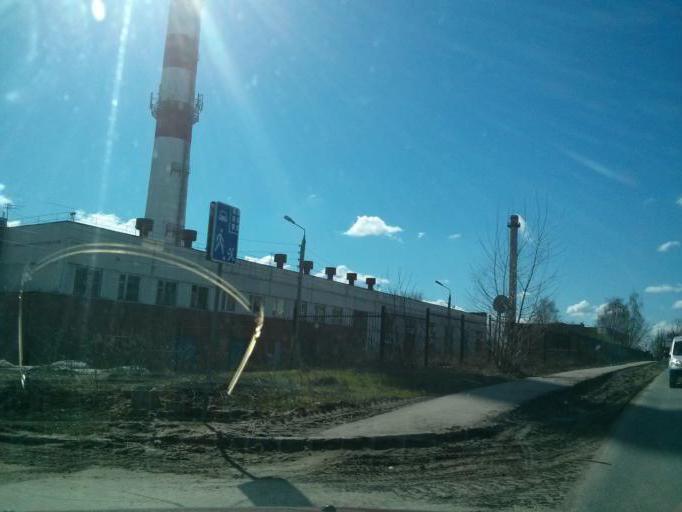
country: RU
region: Nizjnij Novgorod
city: Afonino
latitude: 56.3055
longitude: 44.0719
